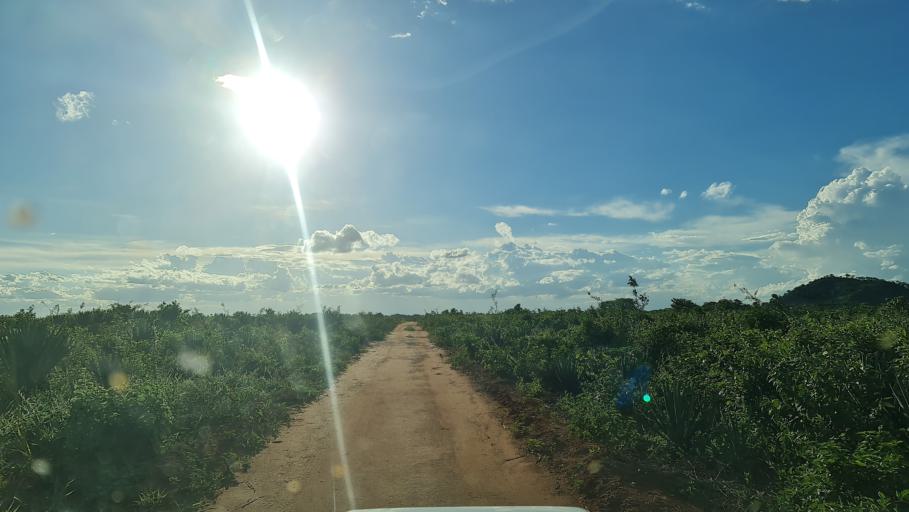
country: MZ
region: Nampula
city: Ilha de Mocambique
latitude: -14.9525
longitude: 40.1835
